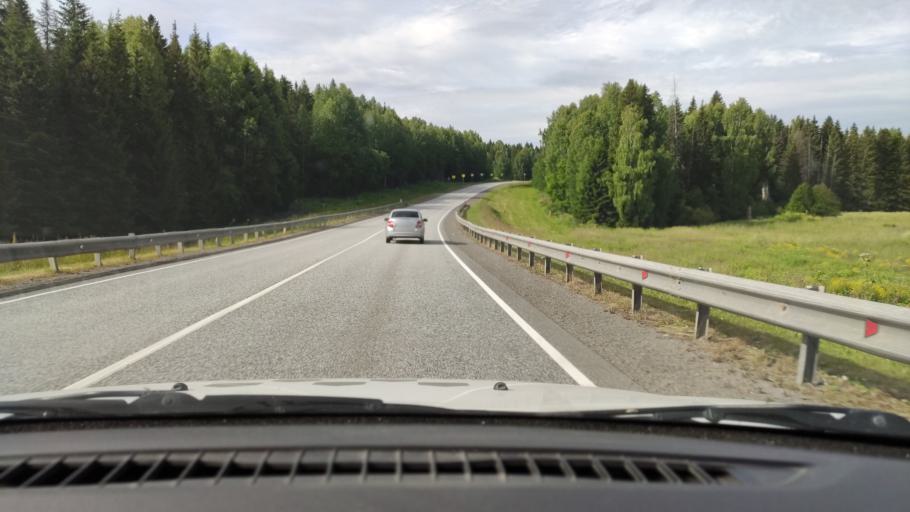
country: RU
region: Perm
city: Pavlovskiy
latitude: 57.8988
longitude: 54.9502
